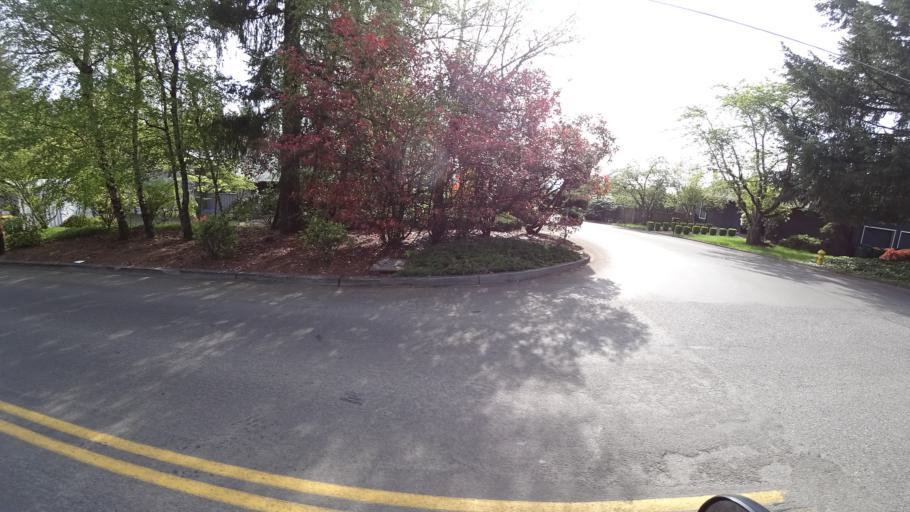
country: US
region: Oregon
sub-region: Washington County
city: Aloha
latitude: 45.4504
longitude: -122.8518
